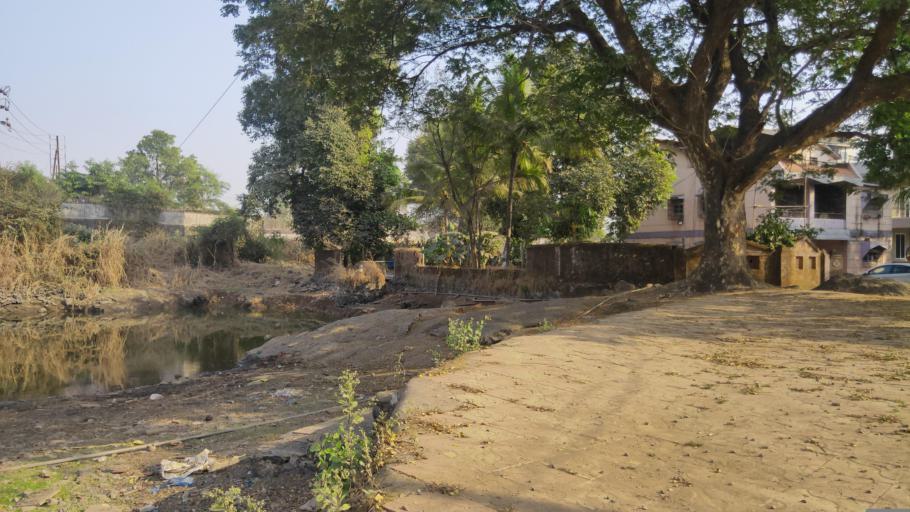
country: IN
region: Maharashtra
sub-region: Thane
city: Bhiwandi
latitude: 19.3523
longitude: 73.1508
